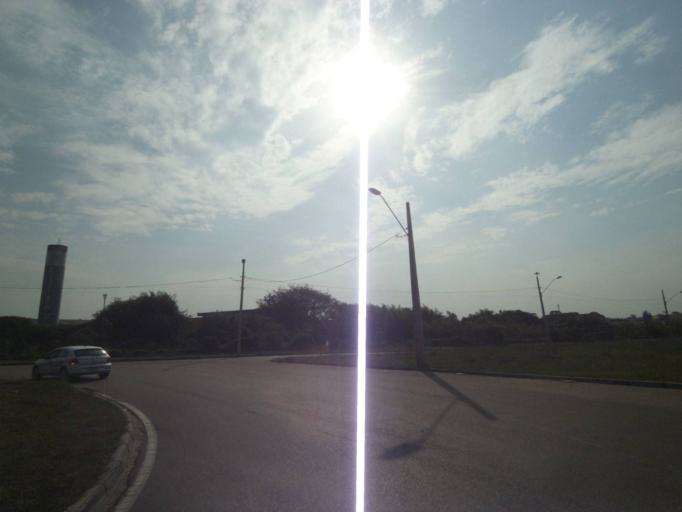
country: BR
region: Parana
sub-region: Sao Jose Dos Pinhais
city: Sao Jose dos Pinhais
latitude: -25.5022
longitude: -49.2110
